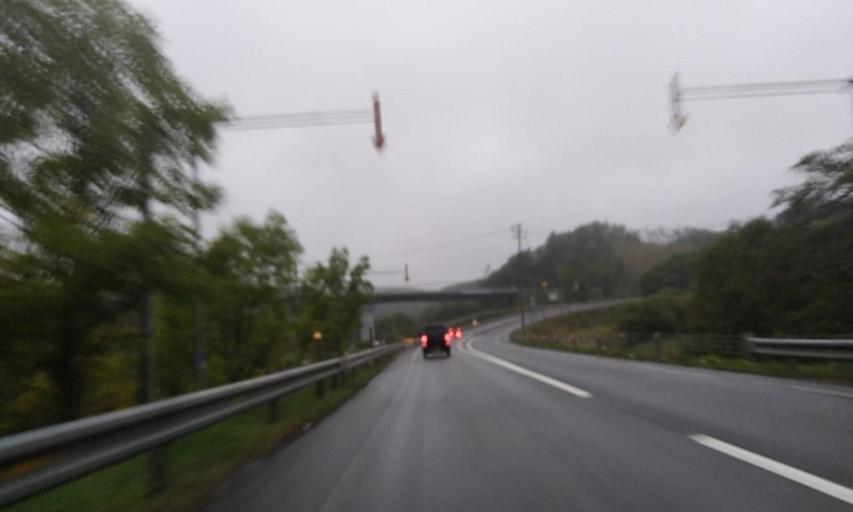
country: JP
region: Hokkaido
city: Kushiro
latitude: 43.0011
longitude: 144.5014
